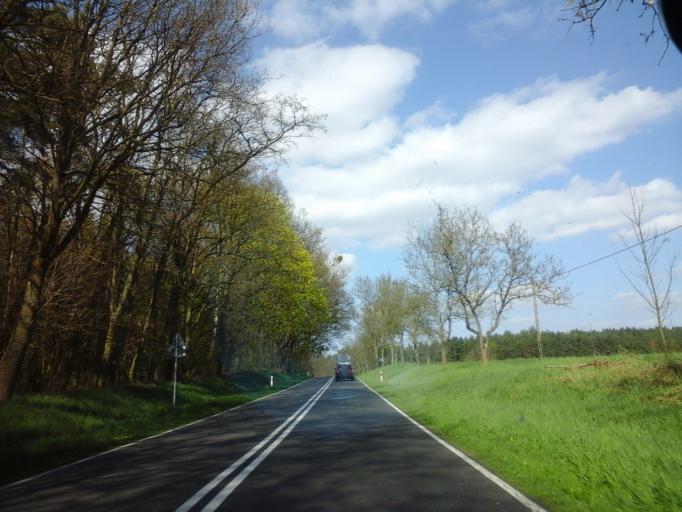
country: PL
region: West Pomeranian Voivodeship
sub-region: Powiat stargardzki
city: Suchan
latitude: 53.2422
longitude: 15.3216
